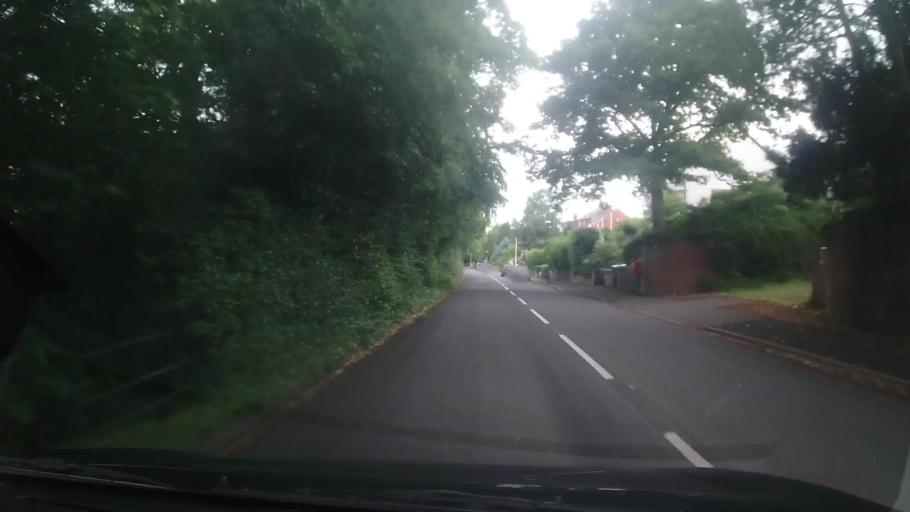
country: GB
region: England
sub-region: Shropshire
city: Shrewsbury
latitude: 52.7188
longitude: -2.7611
